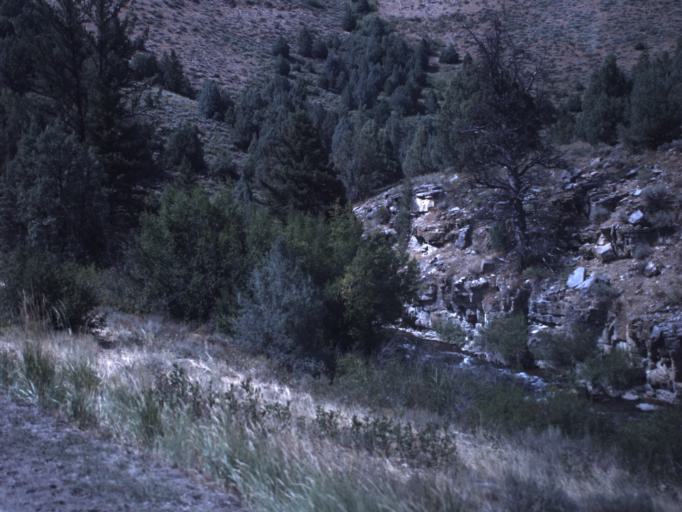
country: US
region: Utah
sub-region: Cache County
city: North Logan
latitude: 41.8360
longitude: -111.5948
